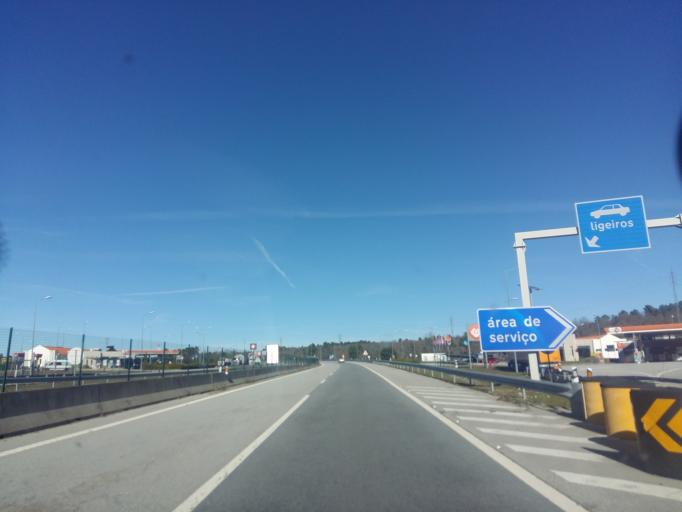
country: PT
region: Guarda
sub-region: Guarda
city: Sequeira
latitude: 40.5426
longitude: -7.2163
